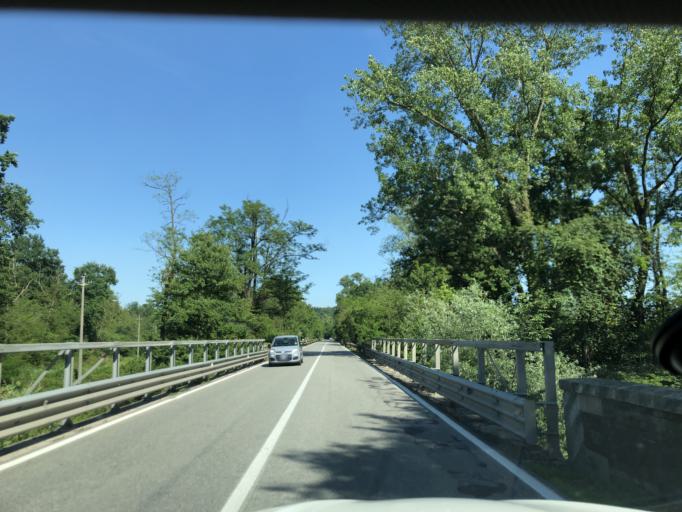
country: IT
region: Lombardy
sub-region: Provincia di Varese
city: Vizzola Ticino
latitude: 45.5913
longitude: 8.6943
